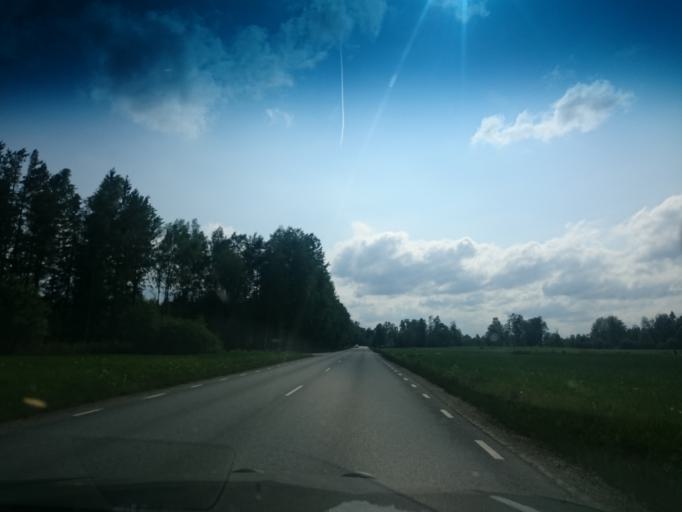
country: SE
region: Joenkoeping
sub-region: Vetlanda Kommun
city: Landsbro
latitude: 57.3908
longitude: 14.9798
